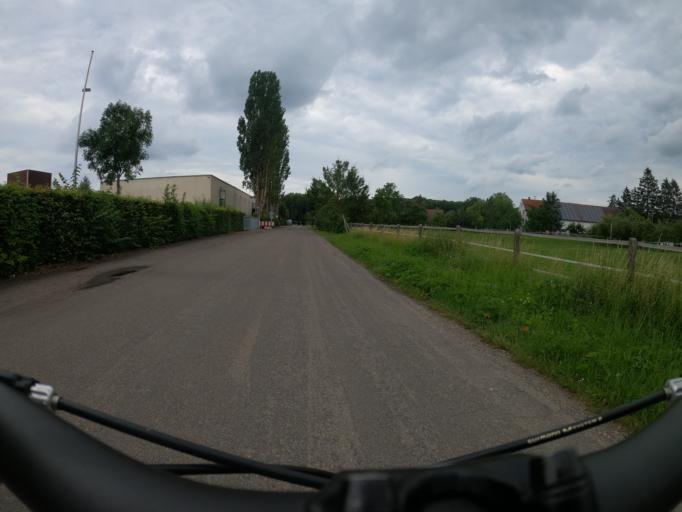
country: DE
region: Bavaria
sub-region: Swabia
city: Neu-Ulm
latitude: 48.4164
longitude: 10.0274
